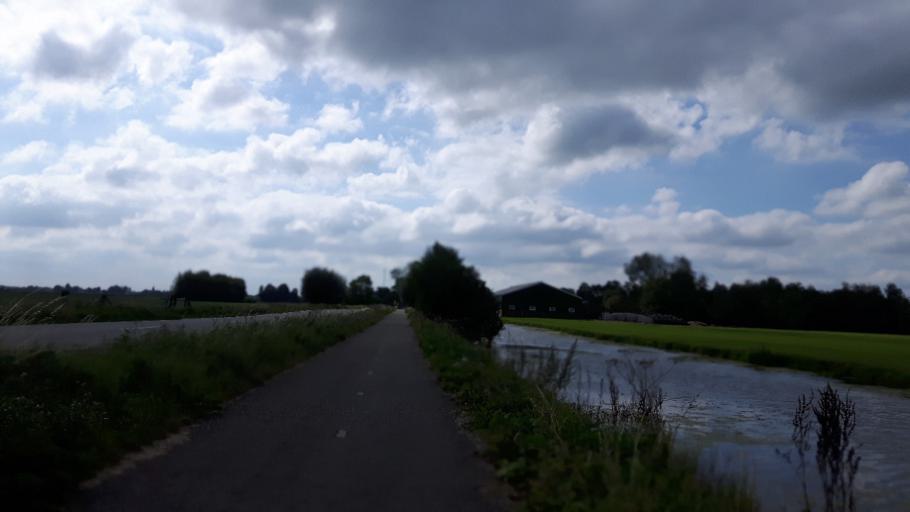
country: NL
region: Utrecht
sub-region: Gemeente Woerden
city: Woerden
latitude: 52.1269
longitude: 4.8536
